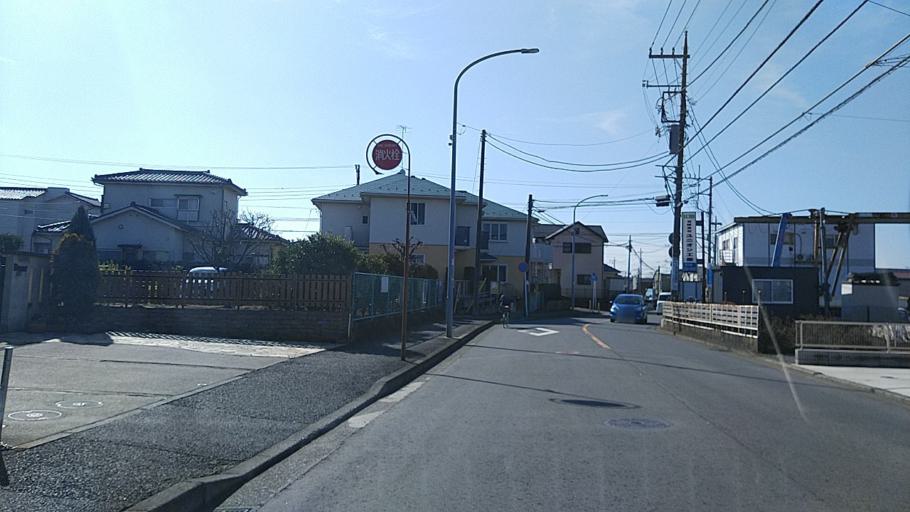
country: JP
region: Kanagawa
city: Fujisawa
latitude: 35.4033
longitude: 139.4948
